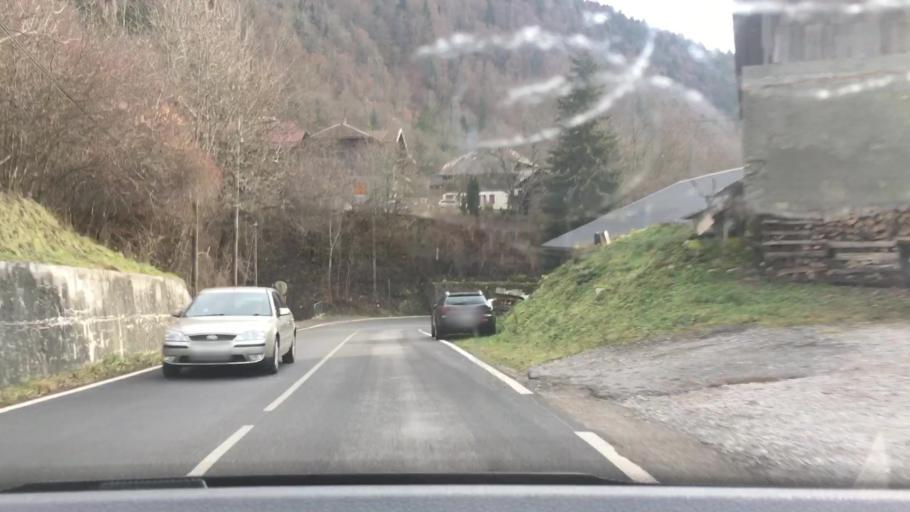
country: FR
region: Rhone-Alpes
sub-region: Departement de la Haute-Savoie
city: Abondance
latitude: 46.2622
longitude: 6.6334
